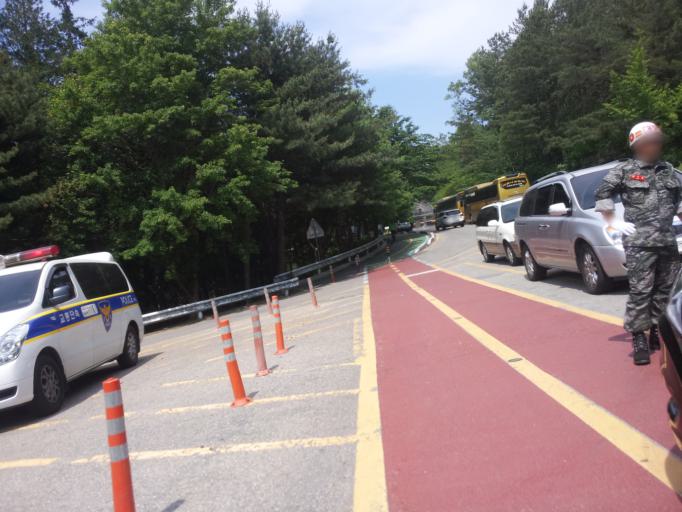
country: KR
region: Daejeon
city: Sintansin
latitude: 36.4720
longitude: 127.4755
